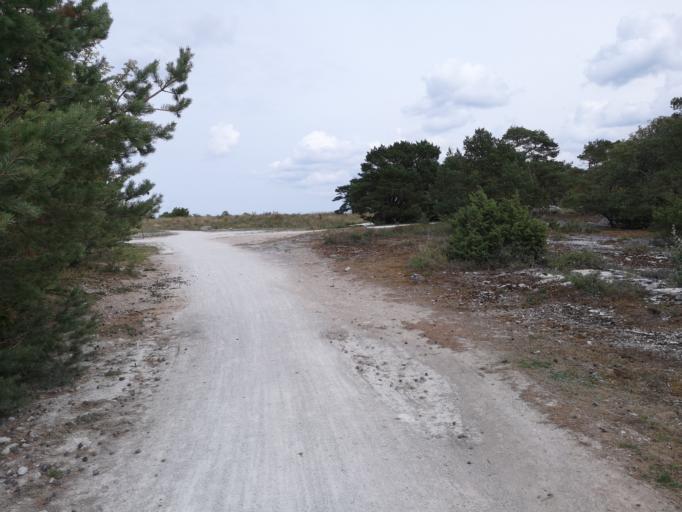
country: SE
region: Gotland
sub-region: Gotland
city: Vibble
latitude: 57.6163
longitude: 18.2610
